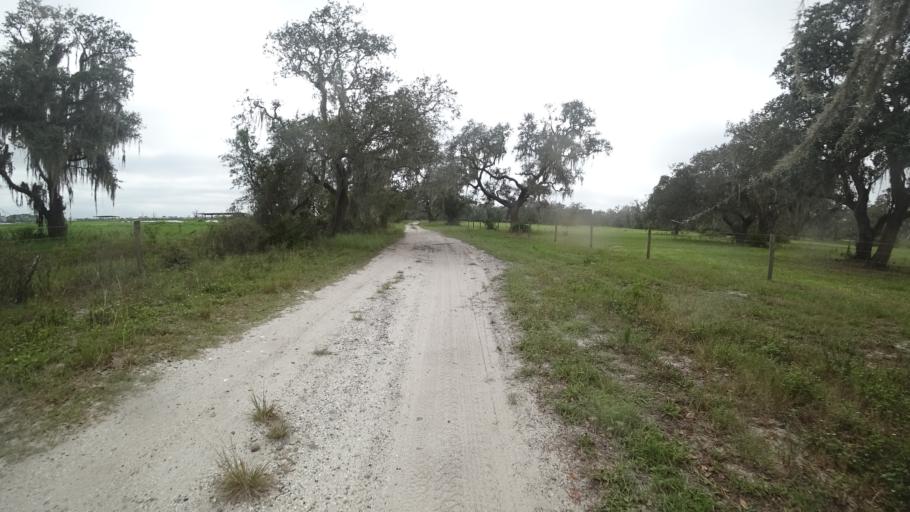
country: US
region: Florida
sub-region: Sarasota County
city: Warm Mineral Springs
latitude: 27.3234
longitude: -82.1378
